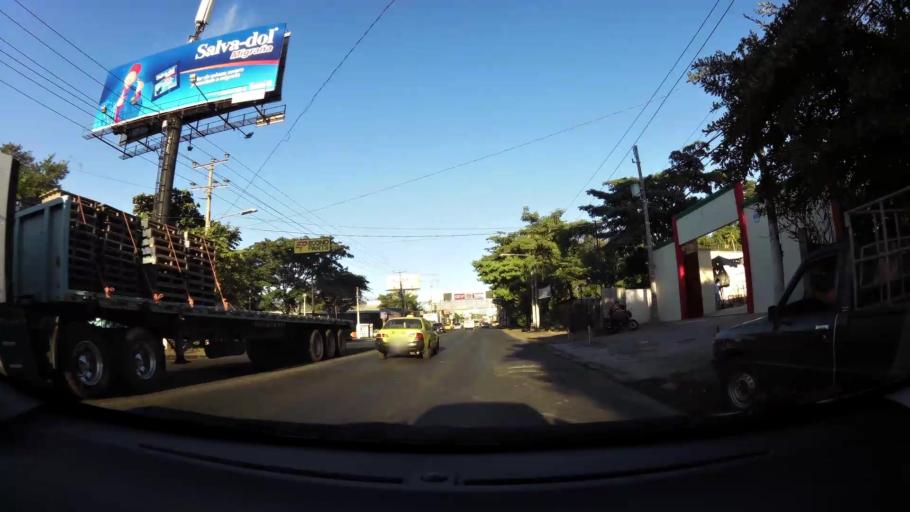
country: SV
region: San Miguel
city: San Miguel
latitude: 13.4653
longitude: -88.1715
